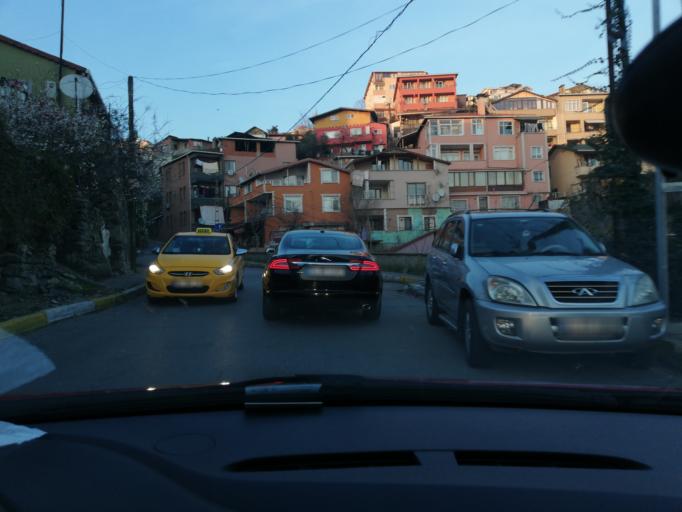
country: TR
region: Istanbul
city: UEskuedar
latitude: 41.0824
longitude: 29.0770
